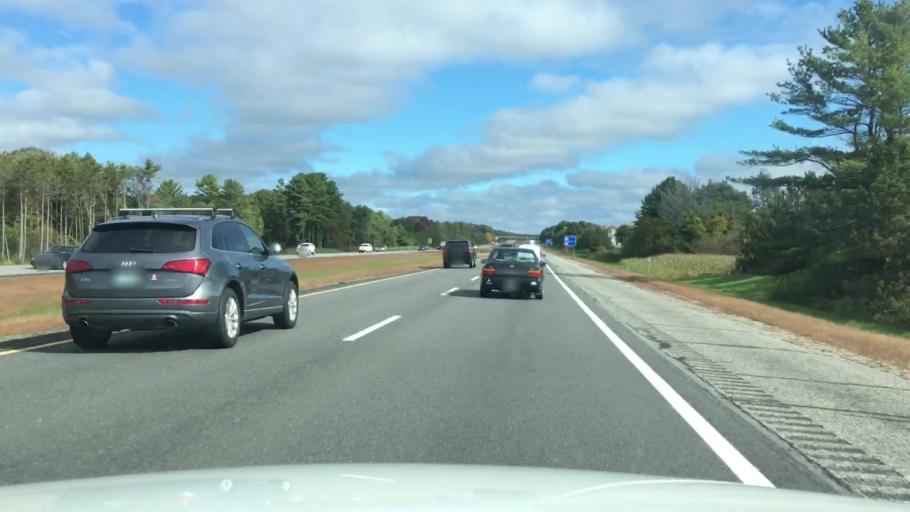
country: US
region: Maine
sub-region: Cumberland County
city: Yarmouth
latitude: 43.8201
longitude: -70.1439
